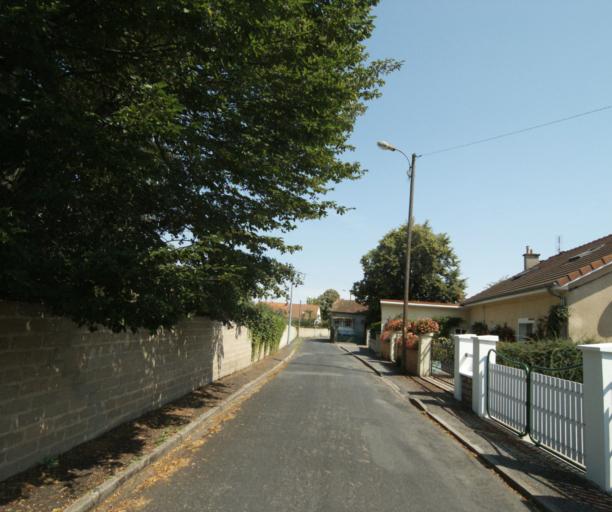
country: FR
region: Bourgogne
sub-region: Departement de Saone-et-Loire
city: Gueugnon
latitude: 46.5987
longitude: 4.0709
